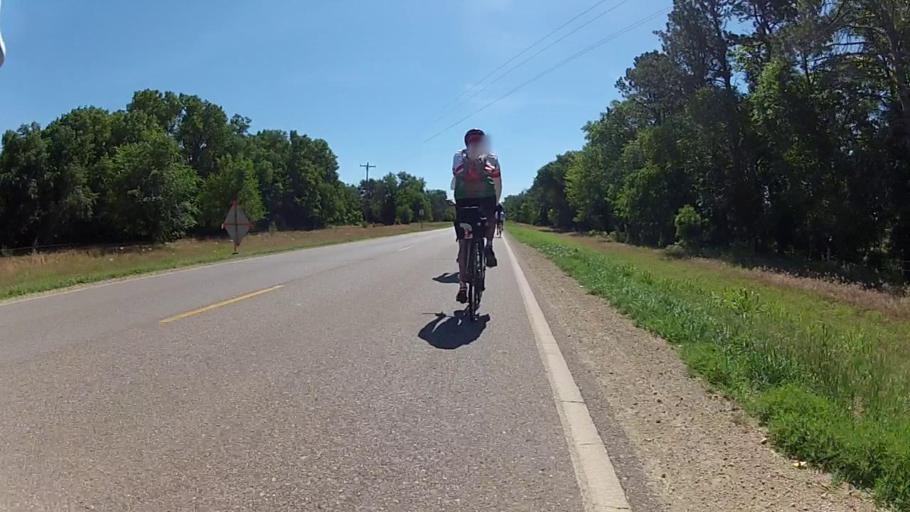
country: US
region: Kansas
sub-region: Barber County
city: Medicine Lodge
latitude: 37.2752
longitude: -98.6036
